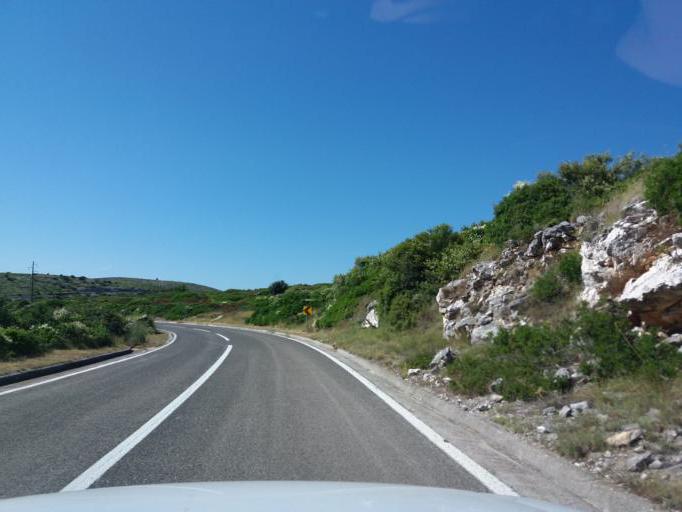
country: HR
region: Zadarska
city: Ugljan
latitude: 44.0298
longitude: 15.0267
